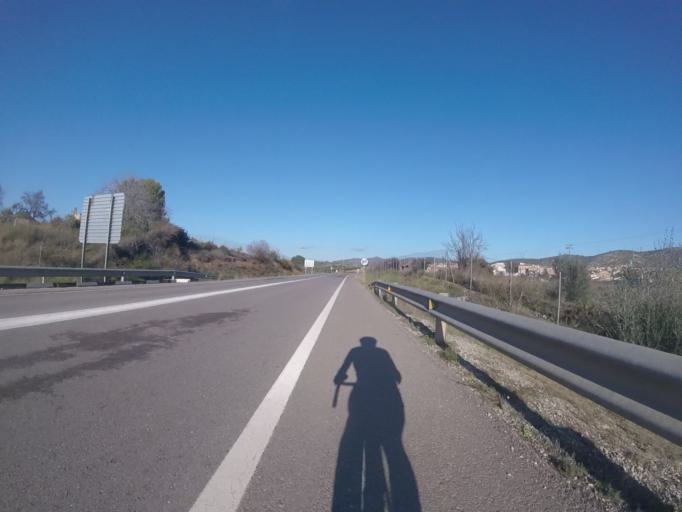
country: ES
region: Valencia
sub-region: Provincia de Castello
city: Cuevas de Vinroma
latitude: 40.3081
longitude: 0.1150
